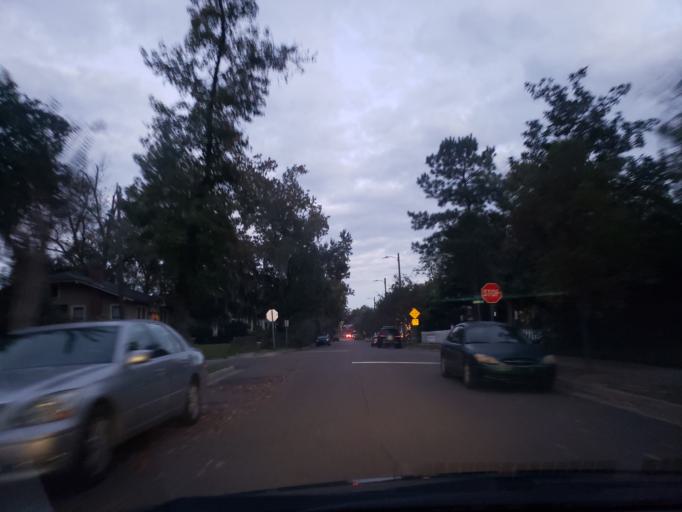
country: US
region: Georgia
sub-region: Chatham County
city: Savannah
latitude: 32.0511
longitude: -81.0872
